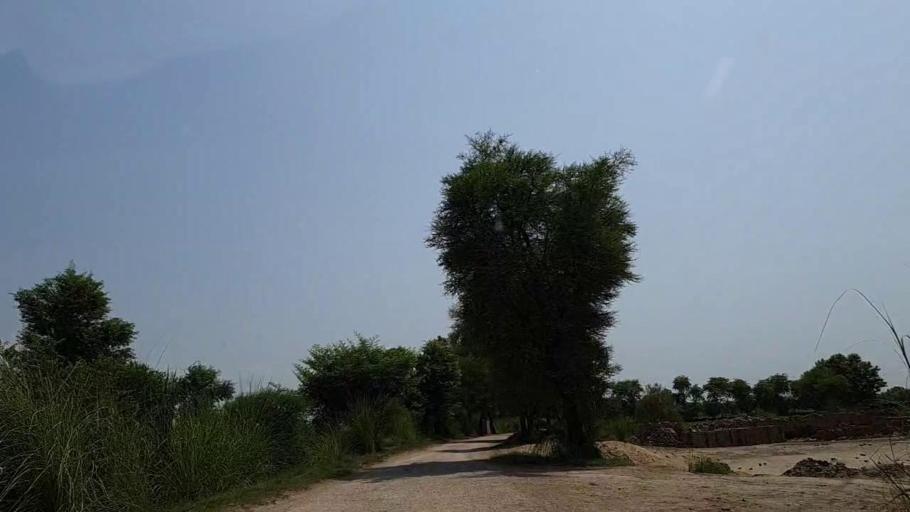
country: PK
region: Sindh
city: Adilpur
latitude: 27.9049
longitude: 69.3628
